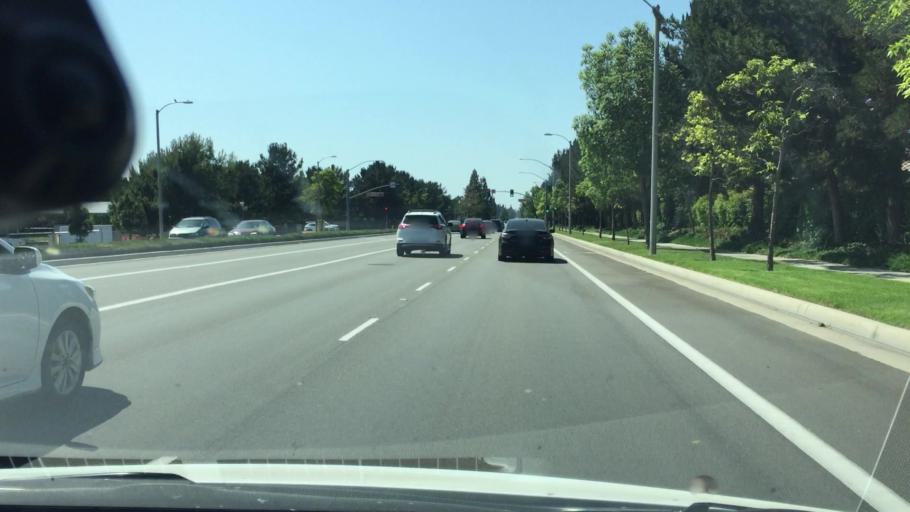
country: US
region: California
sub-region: Orange County
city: North Tustin
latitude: 33.7193
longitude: -117.7812
